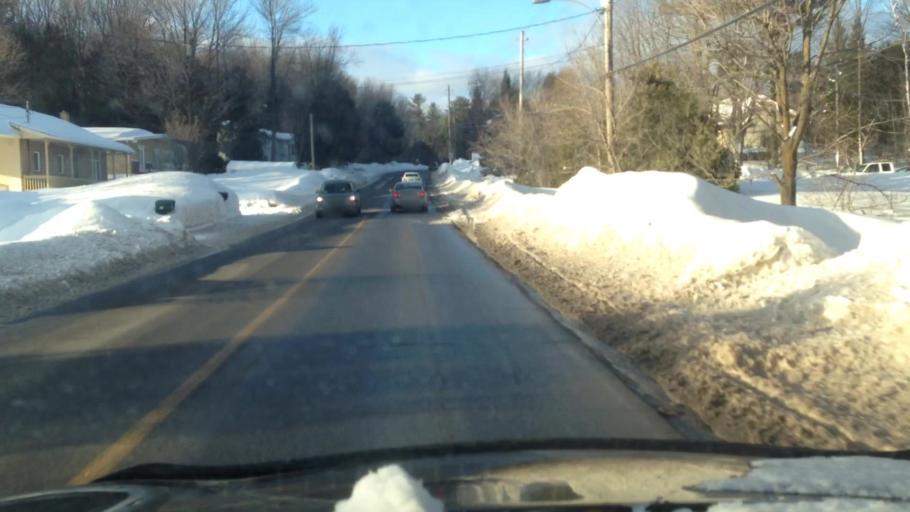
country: CA
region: Quebec
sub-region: Laurentides
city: Saint-Jerome
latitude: 45.8039
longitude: -73.9856
